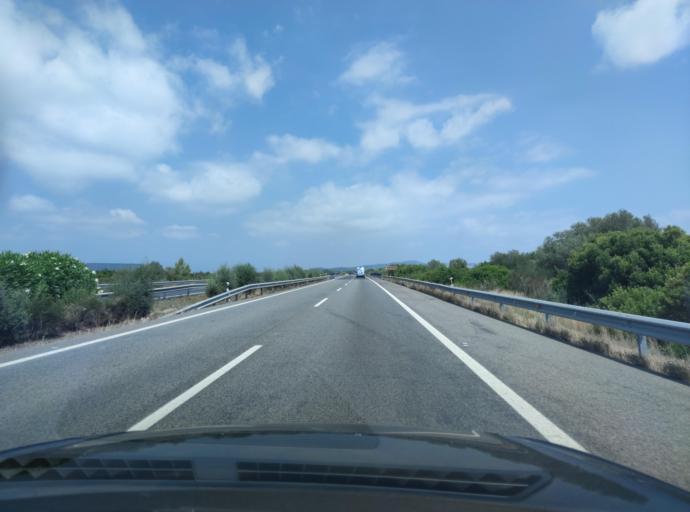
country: ES
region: Catalonia
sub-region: Provincia de Tarragona
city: Alcanar
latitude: 40.5343
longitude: 0.4188
